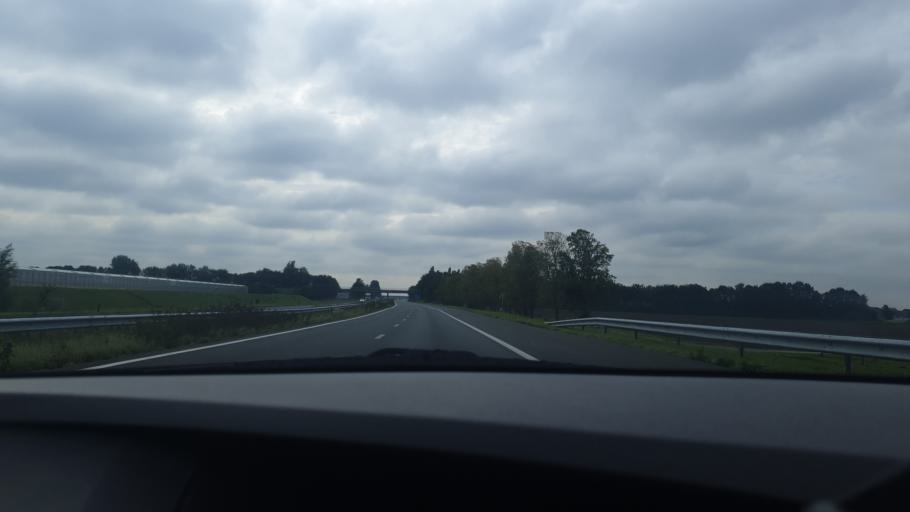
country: NL
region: North Brabant
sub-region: Gemeente Steenbergen
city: Dinteloord
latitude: 51.6356
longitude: 4.3888
